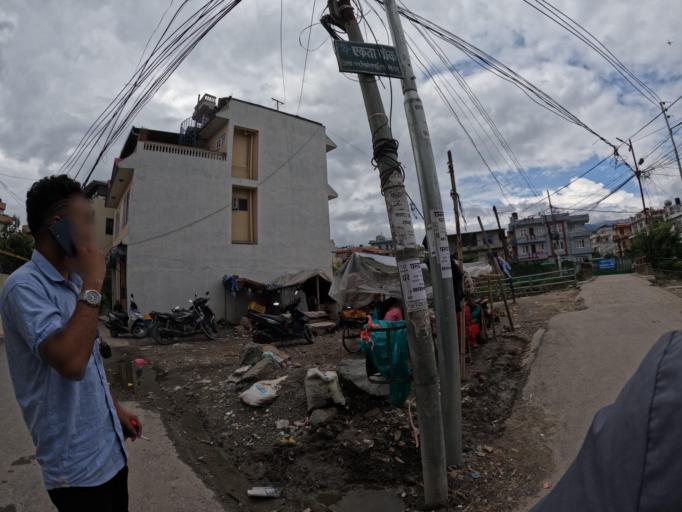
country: NP
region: Central Region
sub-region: Bagmati Zone
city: Kathmandu
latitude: 27.7443
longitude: 85.3207
